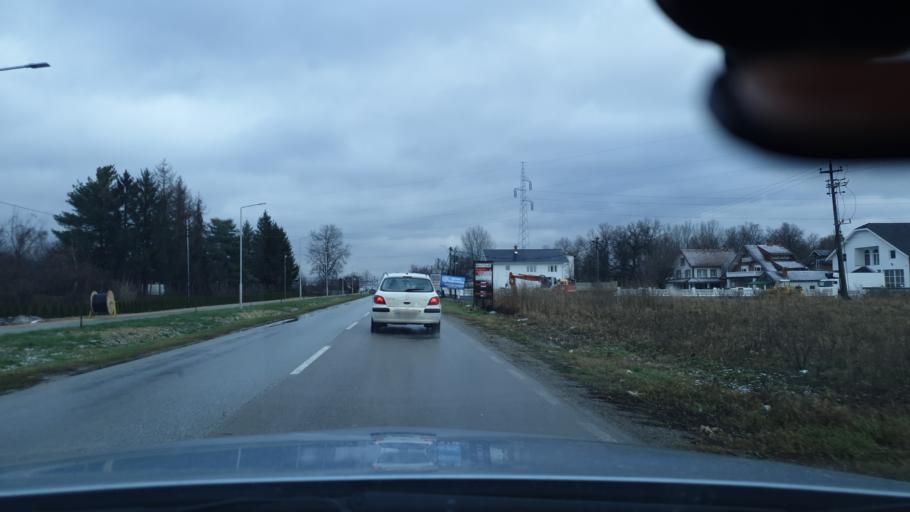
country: RS
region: Central Serbia
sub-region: Branicevski Okrug
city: Petrovac
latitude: 44.3952
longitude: 21.4047
